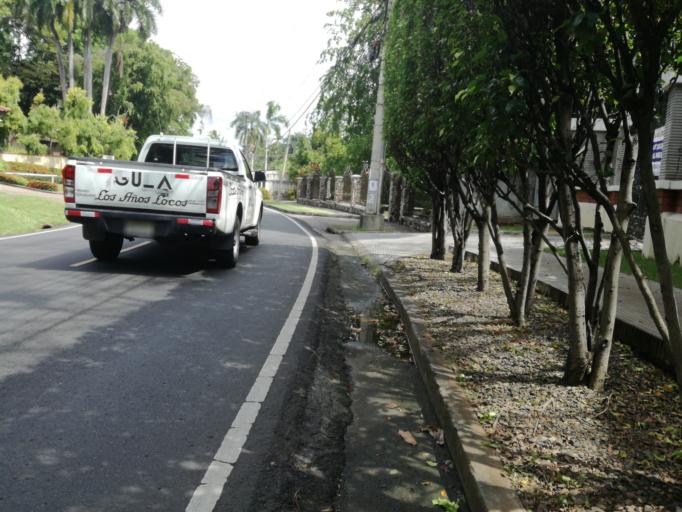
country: PA
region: Panama
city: Panama
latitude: 9.0006
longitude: -79.5023
